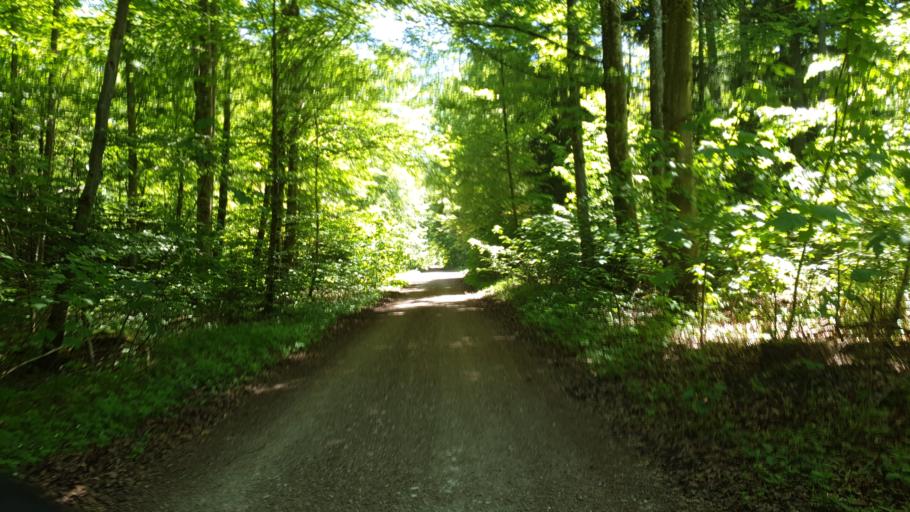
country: DE
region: Bavaria
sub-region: Upper Bavaria
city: Seeshaupt
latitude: 47.7984
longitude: 11.2822
